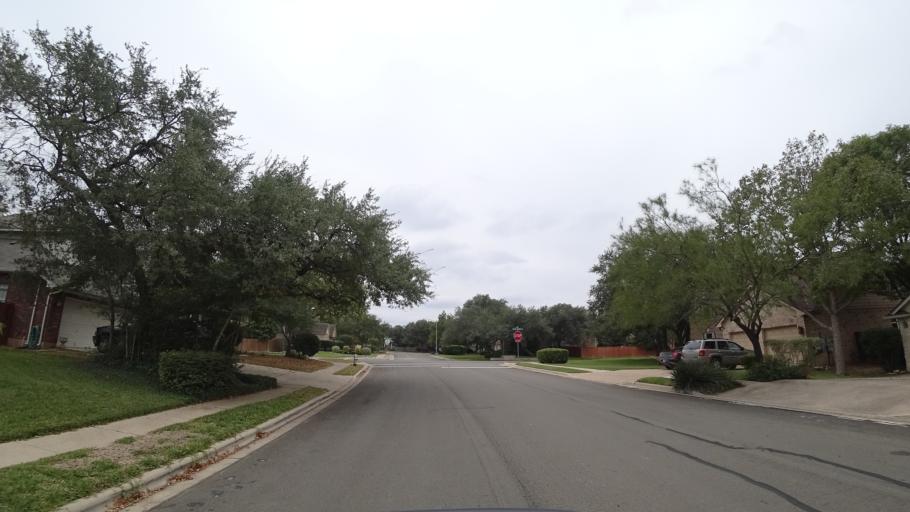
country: US
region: Texas
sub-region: Travis County
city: Shady Hollow
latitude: 30.2088
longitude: -97.8801
